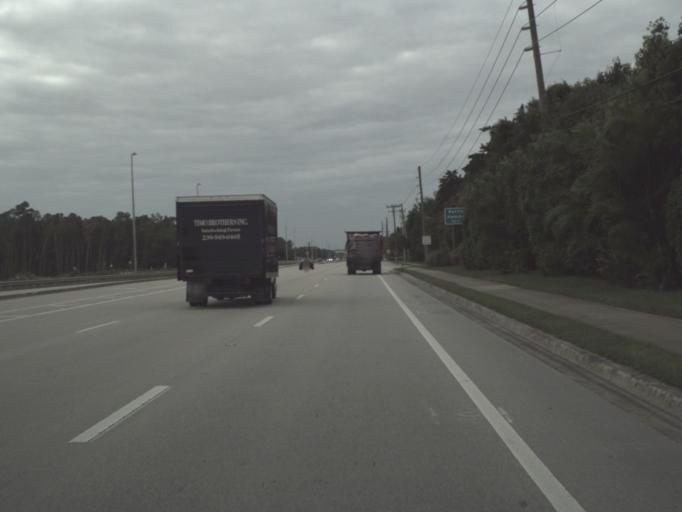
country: US
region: Florida
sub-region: Collier County
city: Lely Resort
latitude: 26.1151
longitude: -81.6872
